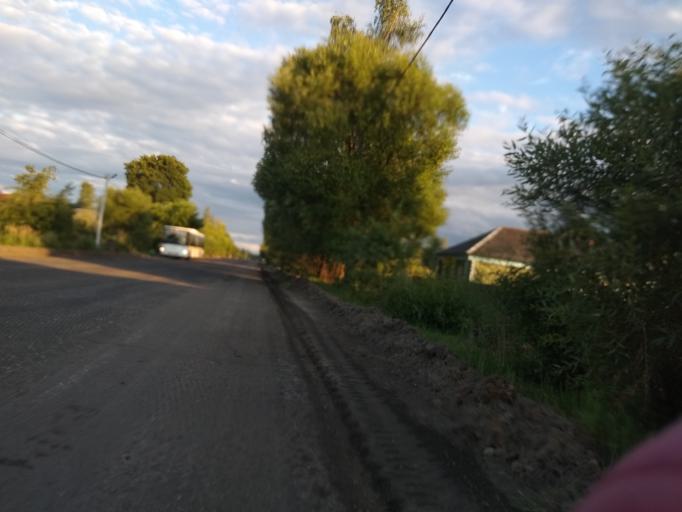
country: RU
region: Moskovskaya
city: Misheronskiy
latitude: 55.6523
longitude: 39.7539
